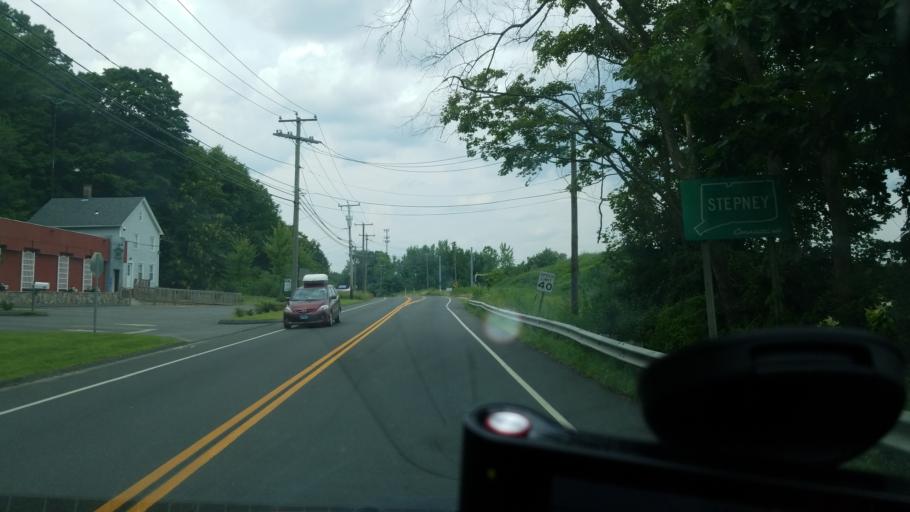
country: US
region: Connecticut
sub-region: Fairfield County
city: Trumbull
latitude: 41.2974
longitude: -73.2473
